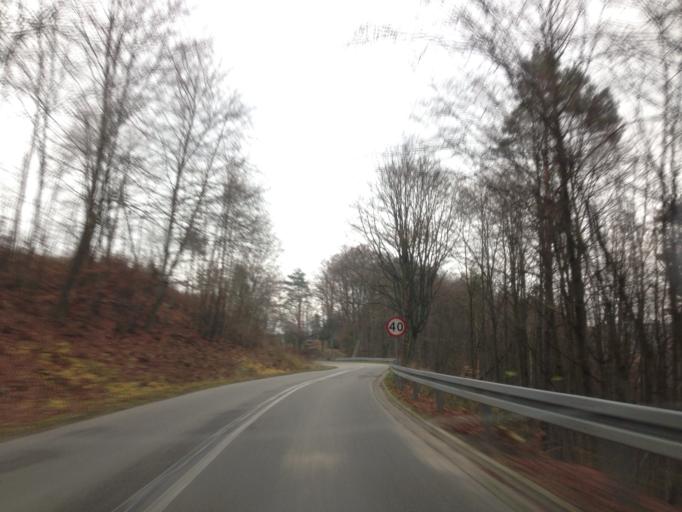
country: PL
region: Pomeranian Voivodeship
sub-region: Powiat gdanski
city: Przywidz
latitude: 54.1876
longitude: 18.3458
